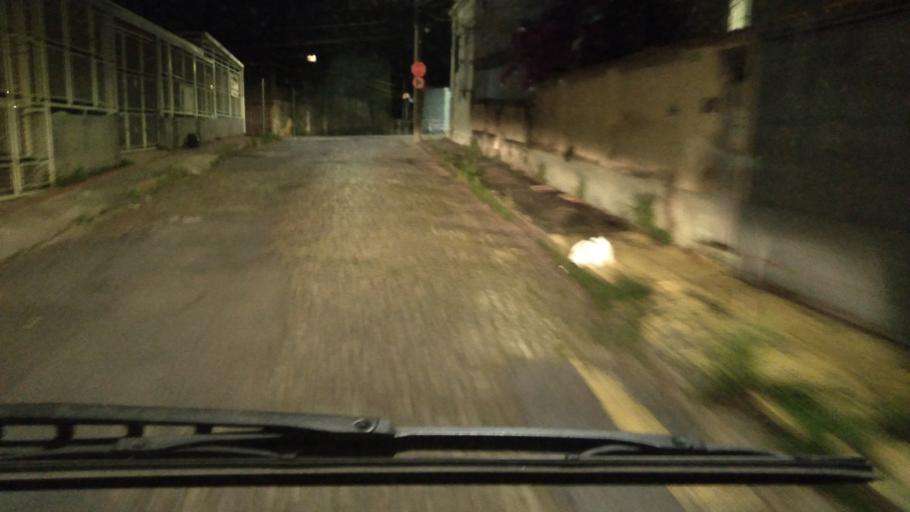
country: BR
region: Minas Gerais
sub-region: Belo Horizonte
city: Belo Horizonte
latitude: -19.9126
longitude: -43.9592
